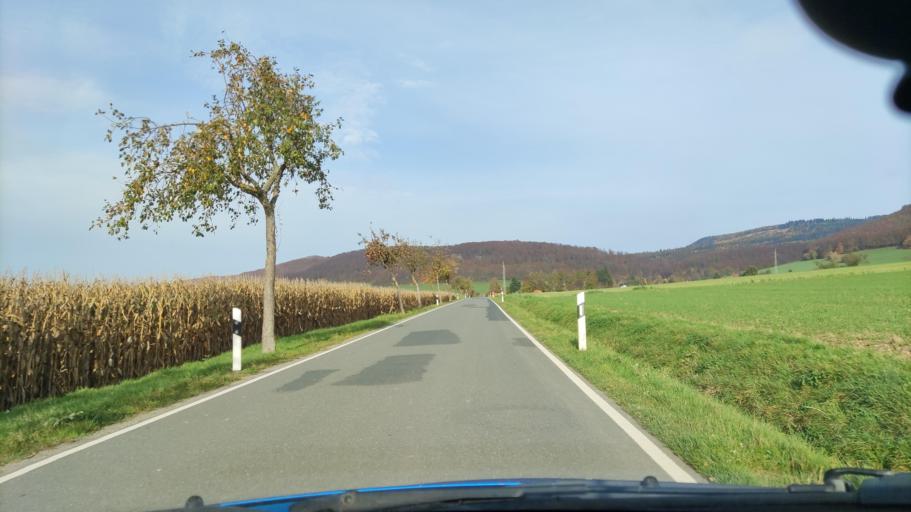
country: DE
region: Lower Saxony
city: Holzen
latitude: 51.9255
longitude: 9.6654
